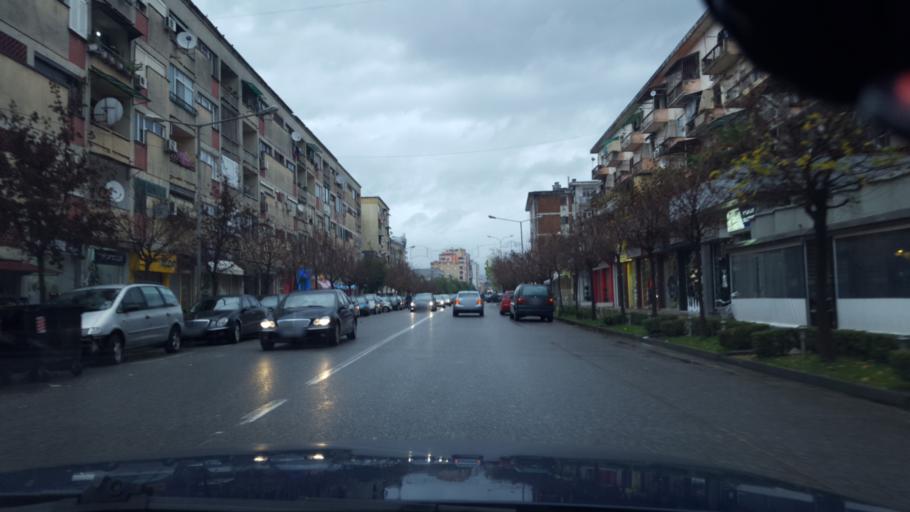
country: AL
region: Shkoder
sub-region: Rrethi i Shkodres
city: Shkoder
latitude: 42.0633
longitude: 19.5072
